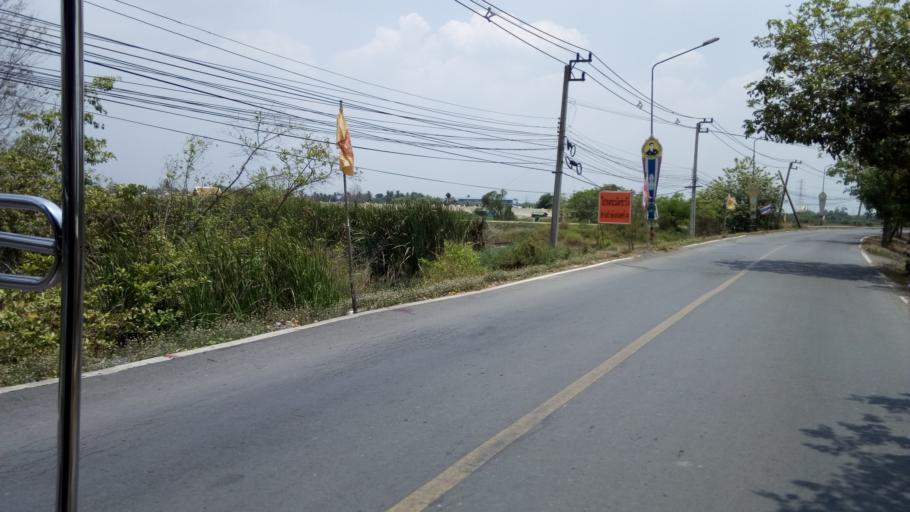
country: TH
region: Pathum Thani
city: Sam Khok
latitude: 14.1122
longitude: 100.5383
